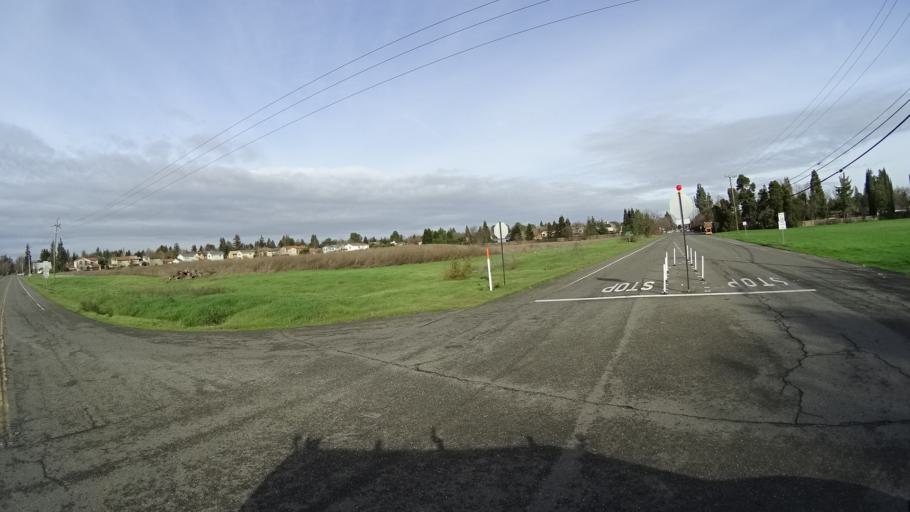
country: US
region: California
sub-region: Yolo County
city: Davis
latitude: 38.5386
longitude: -121.6945
